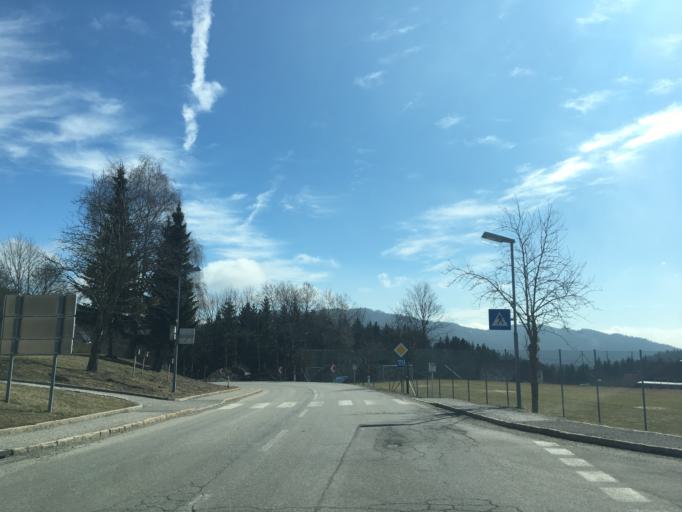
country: AT
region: Upper Austria
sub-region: Politischer Bezirk Perg
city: Sankt Georgen am Walde
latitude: 48.3575
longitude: 14.8975
